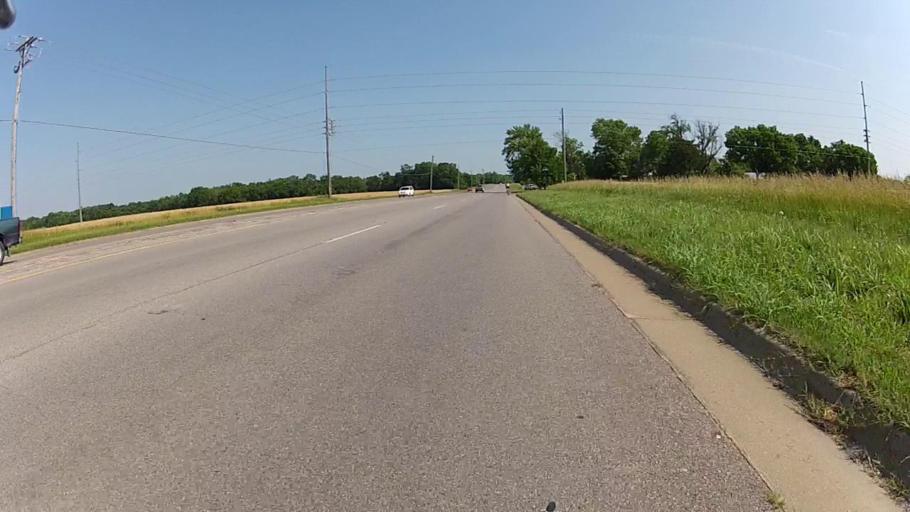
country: US
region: Kansas
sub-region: Montgomery County
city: Independence
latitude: 37.2103
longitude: -95.7107
